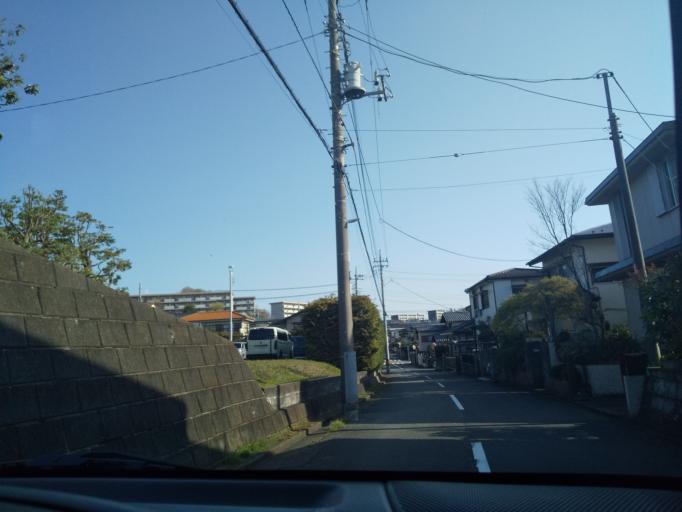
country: JP
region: Tokyo
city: Hino
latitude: 35.6497
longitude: 139.4214
